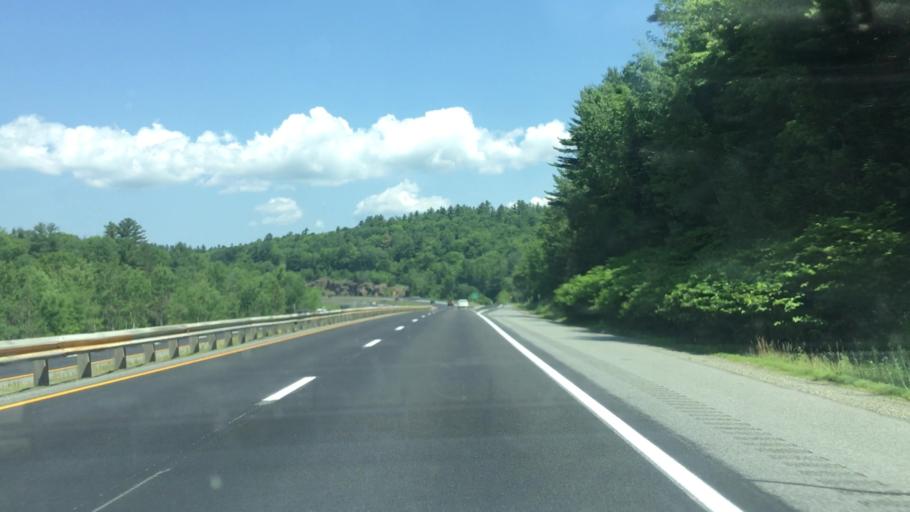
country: US
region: New Hampshire
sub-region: Grafton County
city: Enfield
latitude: 43.5933
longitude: -72.1665
